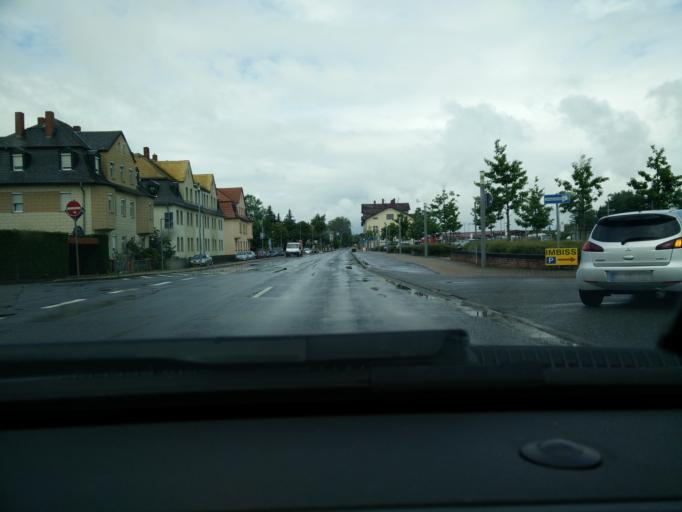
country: DE
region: Saxony
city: Geithain
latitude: 51.0572
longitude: 12.6987
